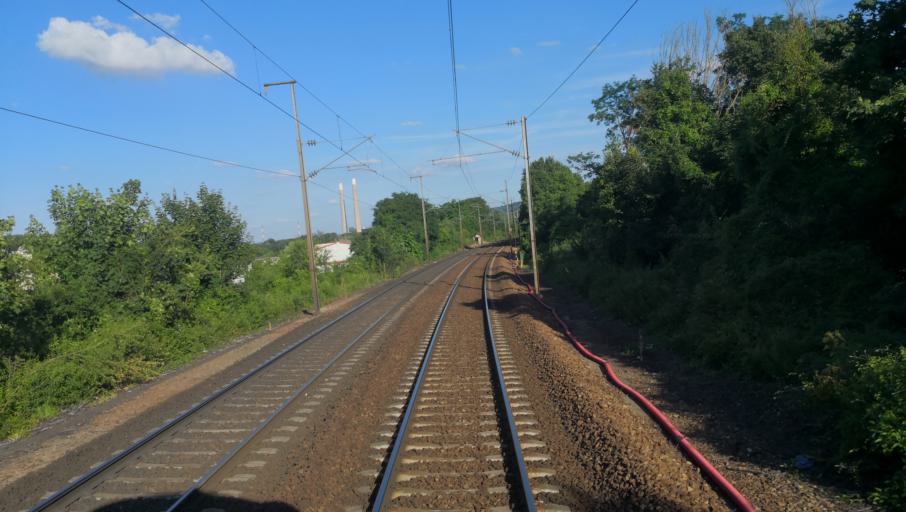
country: FR
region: Ile-de-France
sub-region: Departement des Yvelines
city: Mantes-la-Jolie
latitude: 48.9790
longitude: 1.7272
